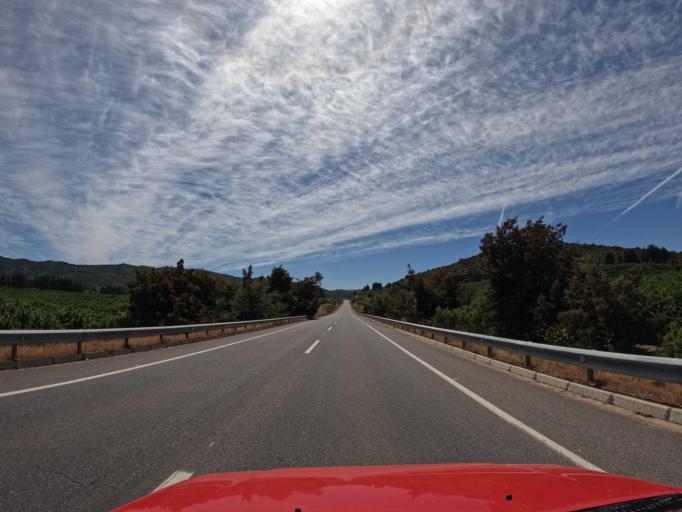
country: CL
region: Maule
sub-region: Provincia de Talca
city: Talca
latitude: -35.2634
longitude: -71.5417
